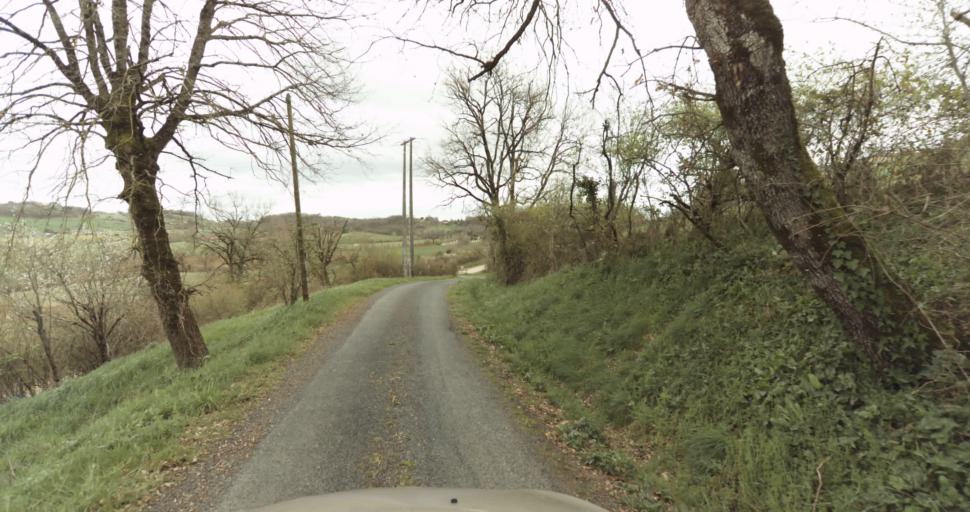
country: FR
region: Midi-Pyrenees
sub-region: Departement du Tarn
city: Puygouzon
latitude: 43.8736
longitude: 2.1699
